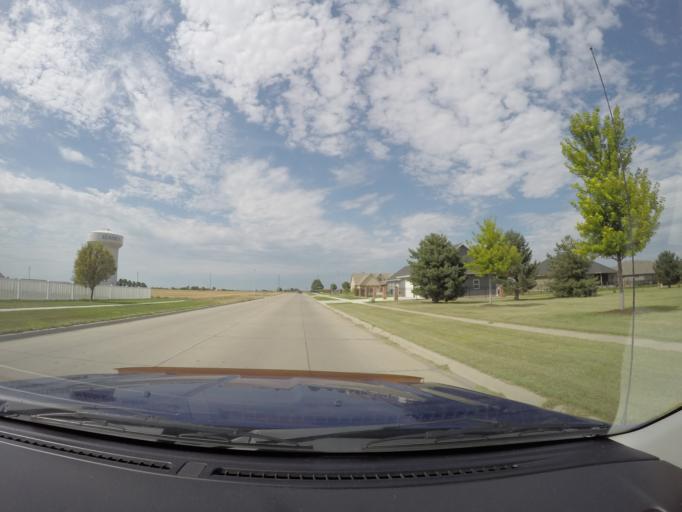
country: US
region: Nebraska
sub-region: Buffalo County
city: Kearney
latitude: 40.7195
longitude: -99.0911
